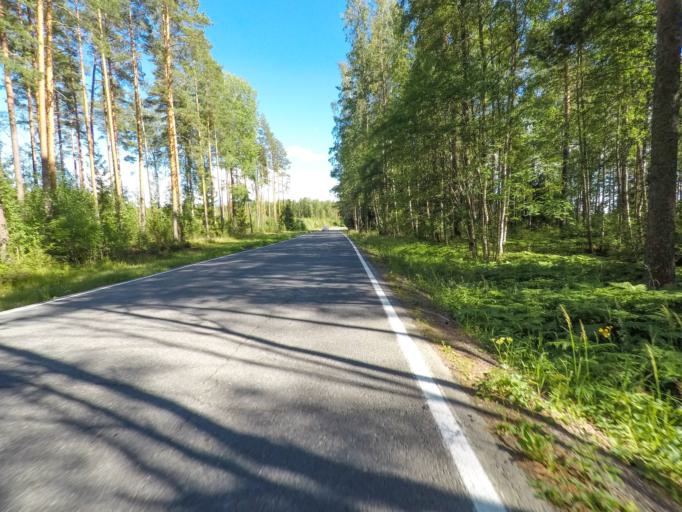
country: FI
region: South Karelia
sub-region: Lappeenranta
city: Taipalsaari
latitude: 61.1797
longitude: 28.0056
